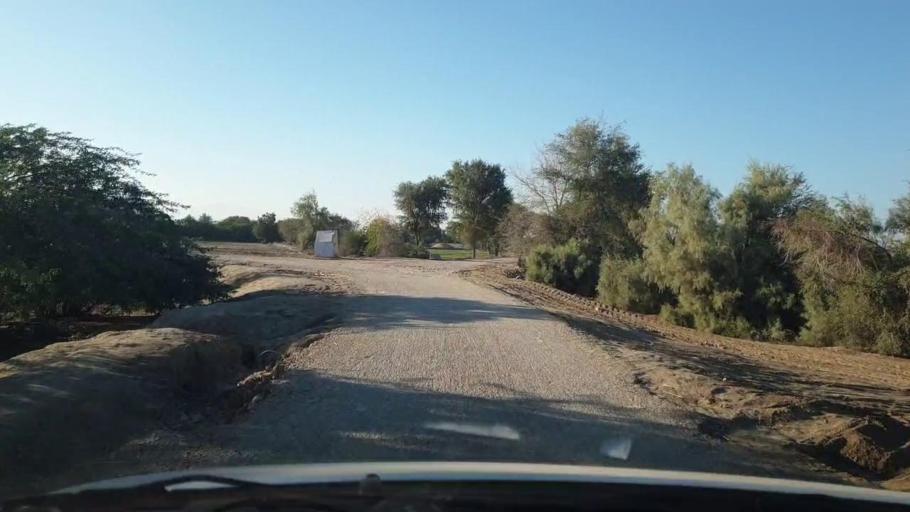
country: PK
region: Sindh
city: Johi
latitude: 26.7752
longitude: 67.4533
